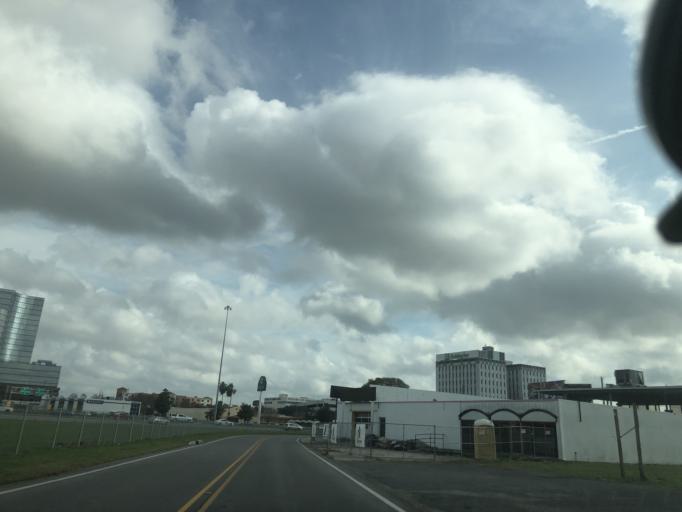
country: US
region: Louisiana
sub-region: Jefferson Parish
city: Metairie
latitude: 29.9956
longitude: -90.1571
